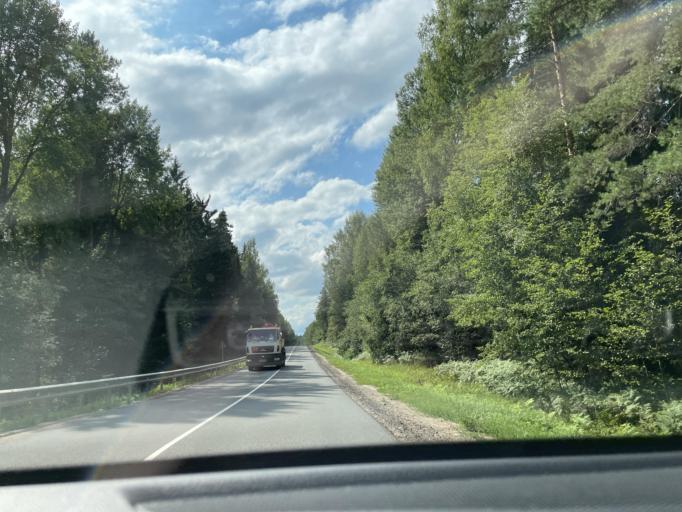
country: RU
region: Novgorod
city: Valday
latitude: 58.0314
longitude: 33.2105
